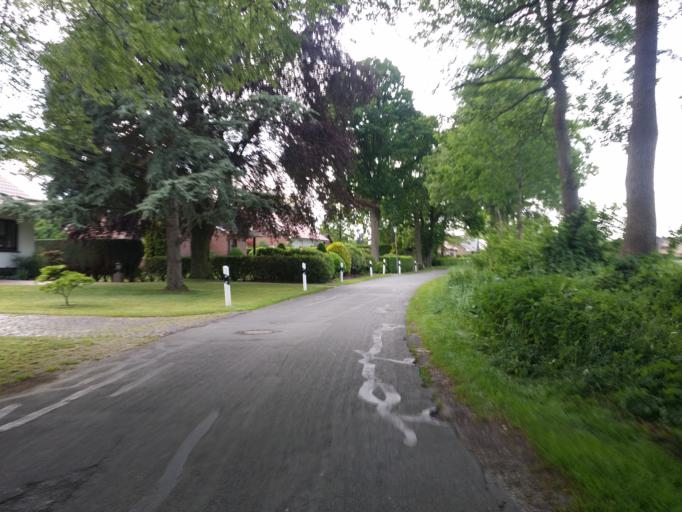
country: DE
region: Lower Saxony
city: Zetel
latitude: 53.3821
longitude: 7.9624
